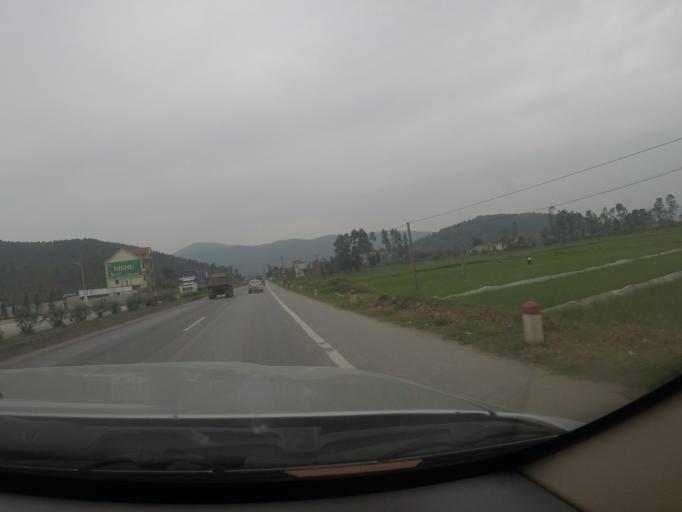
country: VN
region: Nghe An
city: Dien Chau
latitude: 18.9014
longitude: 105.6034
